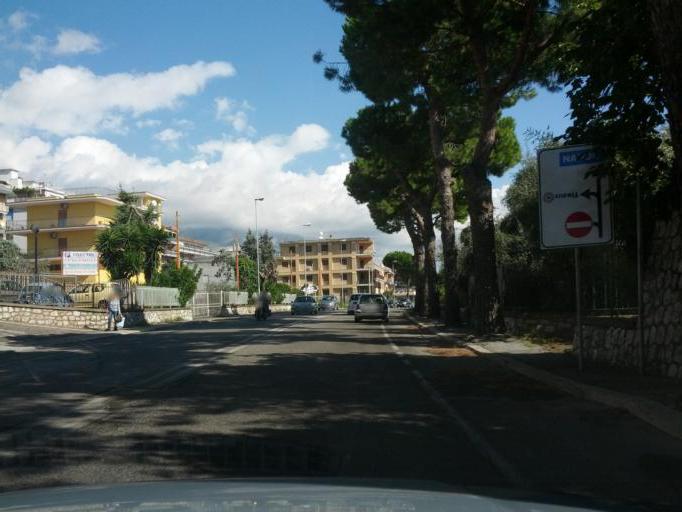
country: IT
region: Latium
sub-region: Provincia di Latina
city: Formia
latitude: 41.2521
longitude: 13.5989
